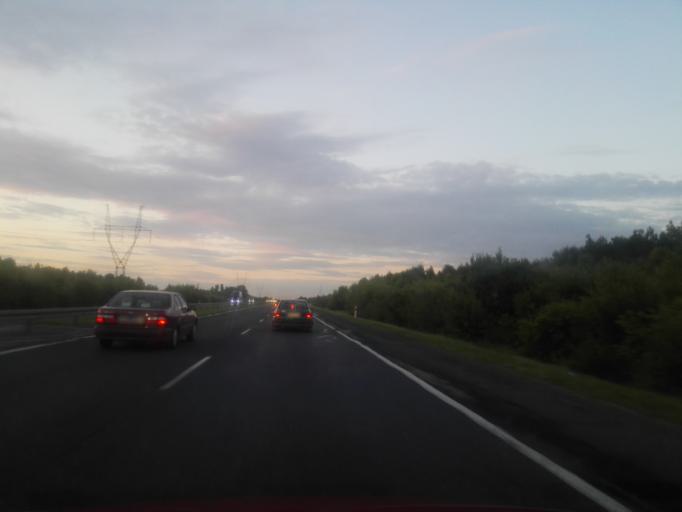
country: PL
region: Lodz Voivodeship
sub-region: Powiat radomszczanski
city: Radomsko
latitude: 51.1160
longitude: 19.3986
